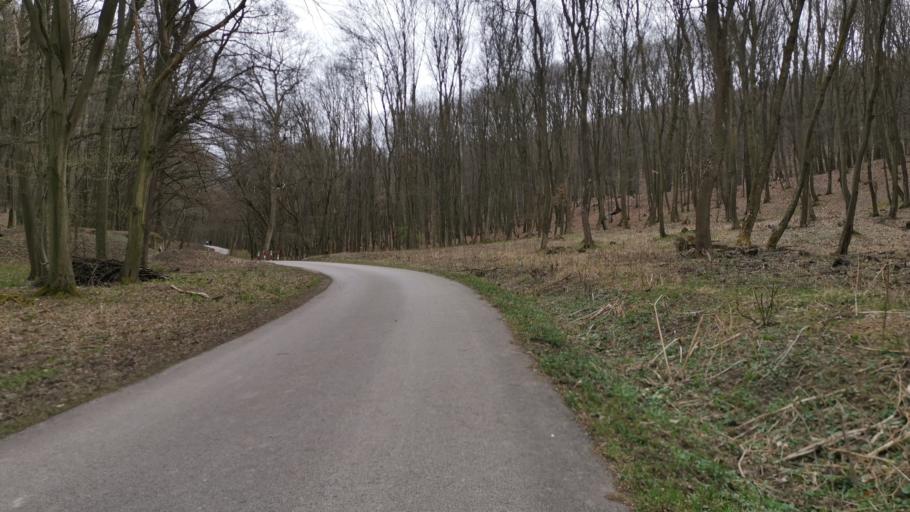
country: CZ
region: South Moravian
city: Sudomerice
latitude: 48.8194
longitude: 17.3039
